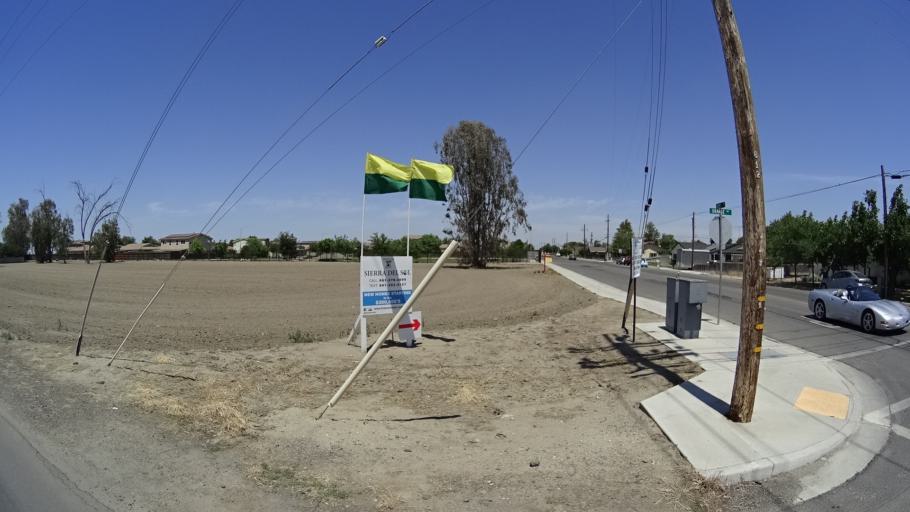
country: US
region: California
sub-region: Kings County
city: Corcoran
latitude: 36.1091
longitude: -119.5722
